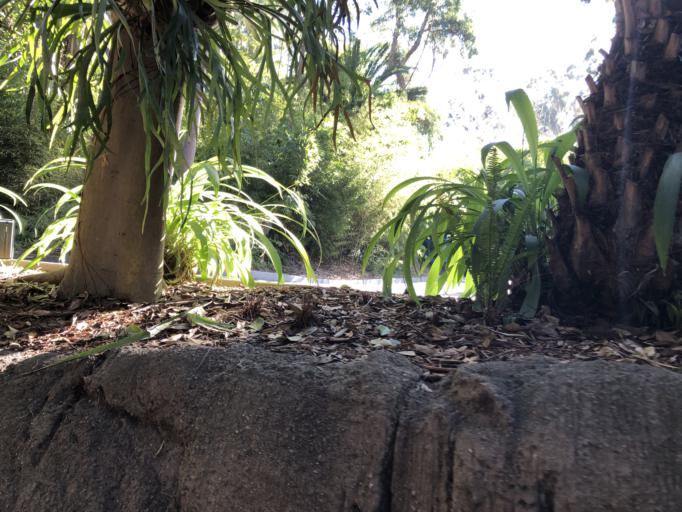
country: US
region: California
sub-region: San Diego County
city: San Diego
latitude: 32.7337
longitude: -117.1517
